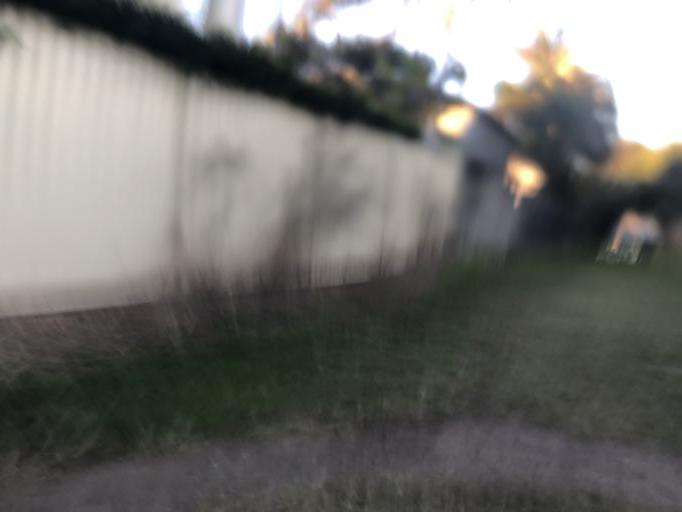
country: AU
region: New South Wales
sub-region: Coffs Harbour
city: Coffs Harbour
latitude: -30.2912
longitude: 153.1372
